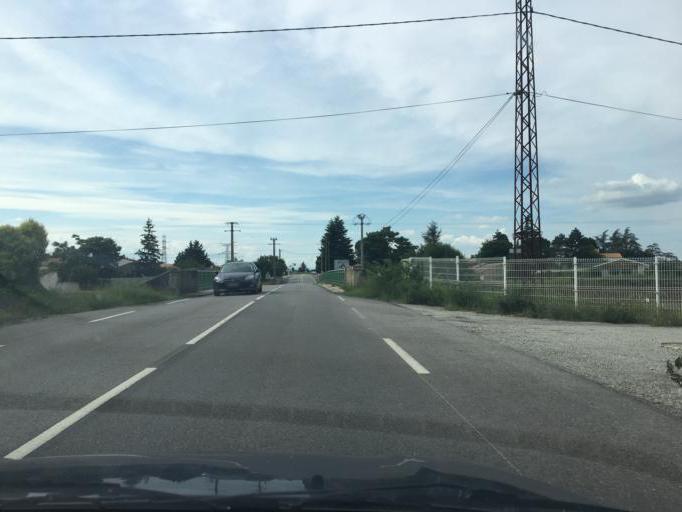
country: FR
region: Rhone-Alpes
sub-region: Departement de la Drome
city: Chateauneuf-sur-Isere
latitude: 45.0181
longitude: 4.9371
